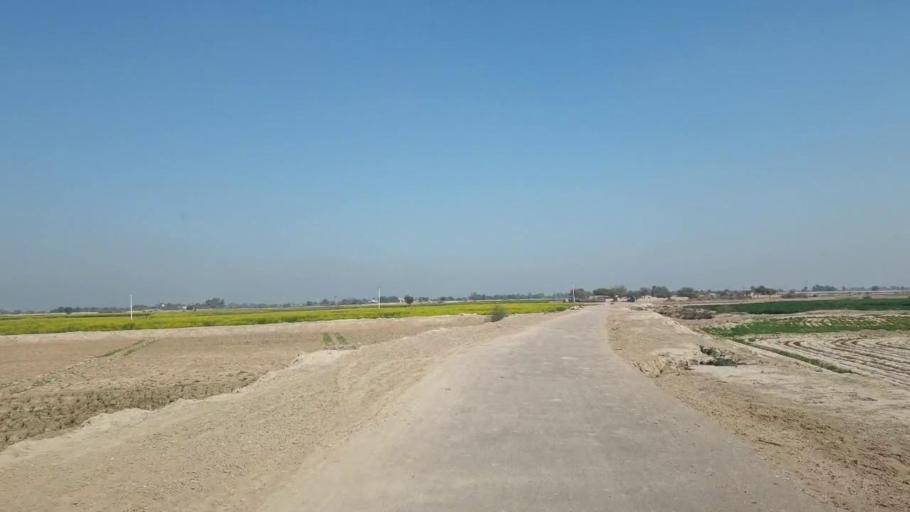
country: PK
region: Sindh
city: Shahpur Chakar
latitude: 26.1216
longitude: 68.6067
